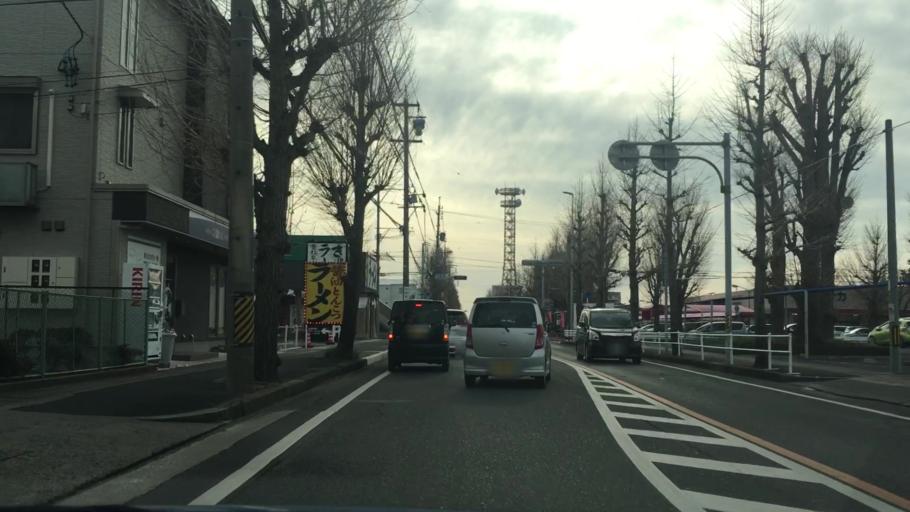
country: JP
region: Aichi
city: Toyohashi
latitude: 34.7377
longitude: 137.3785
